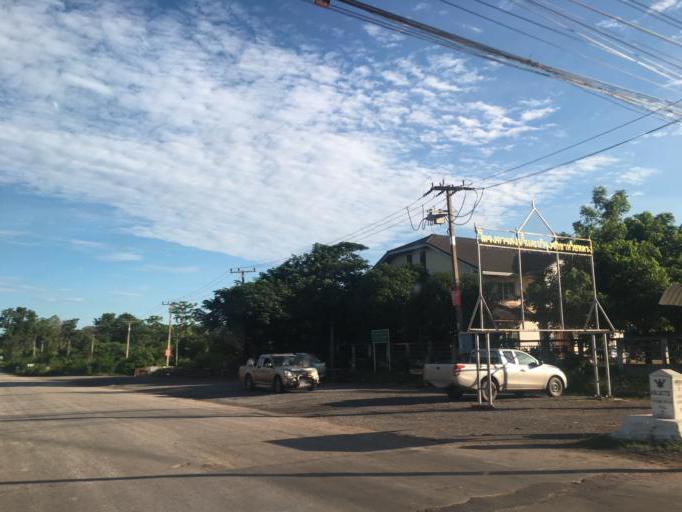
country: TH
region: Changwat Udon Thani
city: Kut Chap
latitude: 17.3364
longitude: 102.6604
